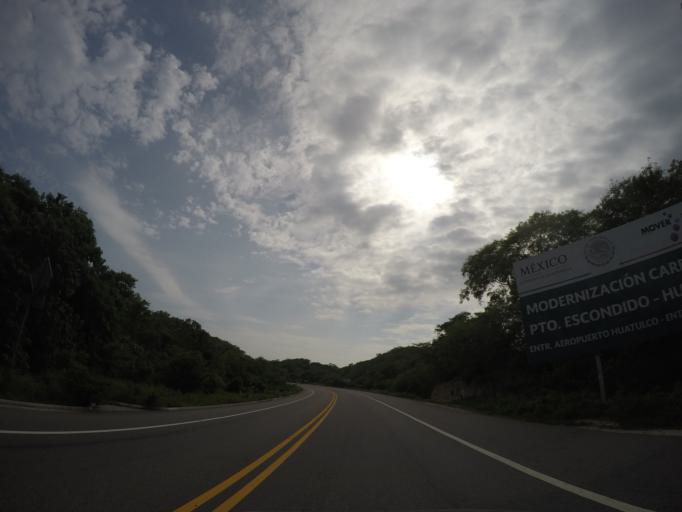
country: MX
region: Oaxaca
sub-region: Santa Maria Huatulco
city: Sector H Tres
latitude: 15.7813
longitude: -96.1630
